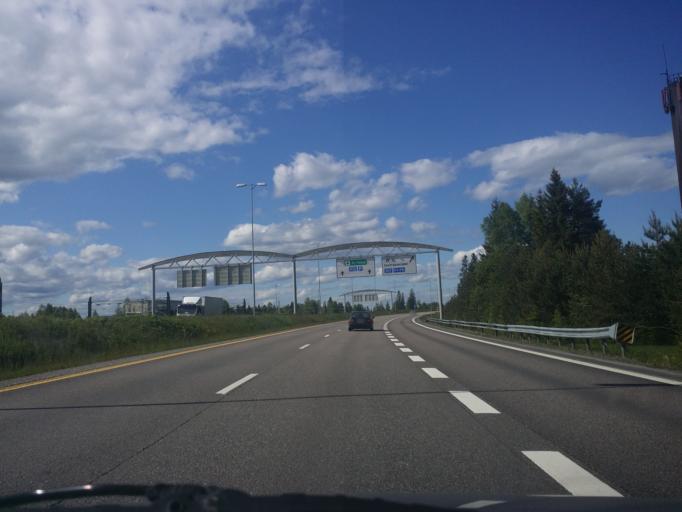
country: NO
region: Akershus
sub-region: Nannestad
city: Teigebyen
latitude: 60.1805
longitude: 11.0938
